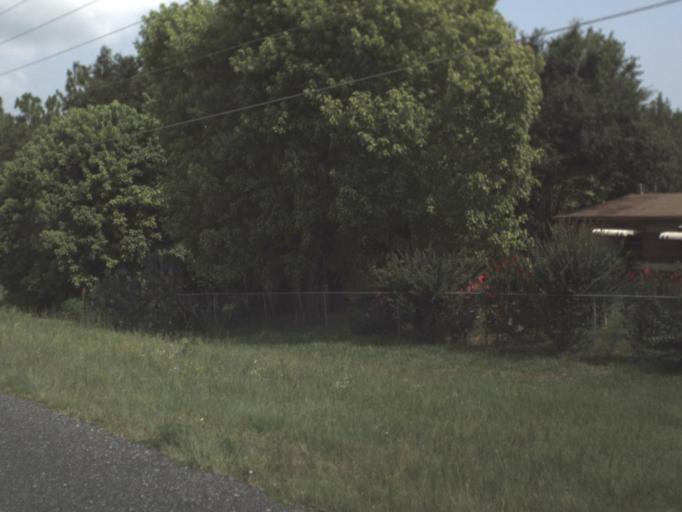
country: US
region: Florida
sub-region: Levy County
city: East Bronson
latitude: 29.4122
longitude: -82.5441
